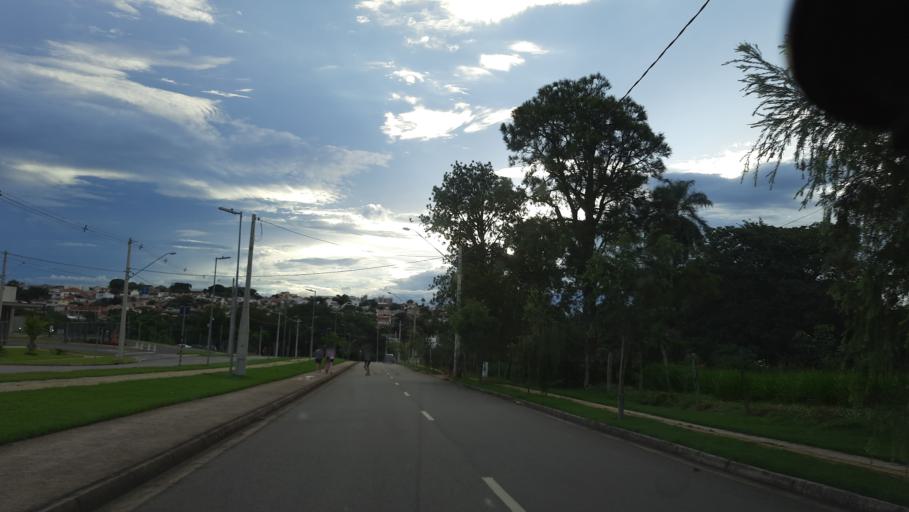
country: BR
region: Sao Paulo
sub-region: Sao Joao Da Boa Vista
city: Sao Joao da Boa Vista
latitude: -21.9625
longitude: -46.7838
